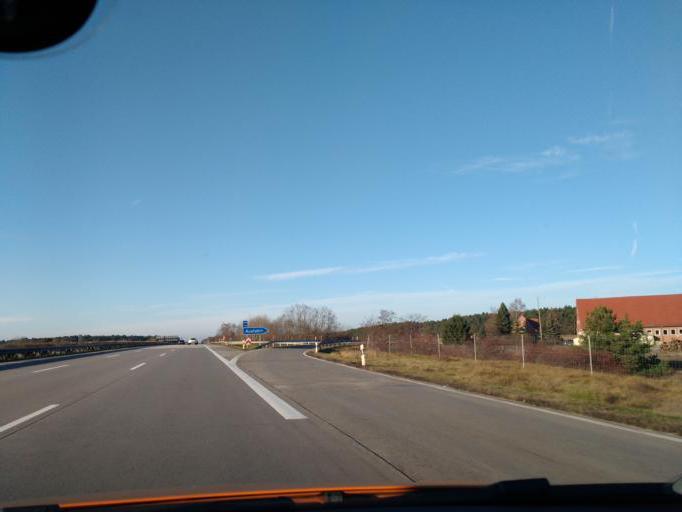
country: DE
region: Brandenburg
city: Ziesar
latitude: 52.2488
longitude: 12.2616
